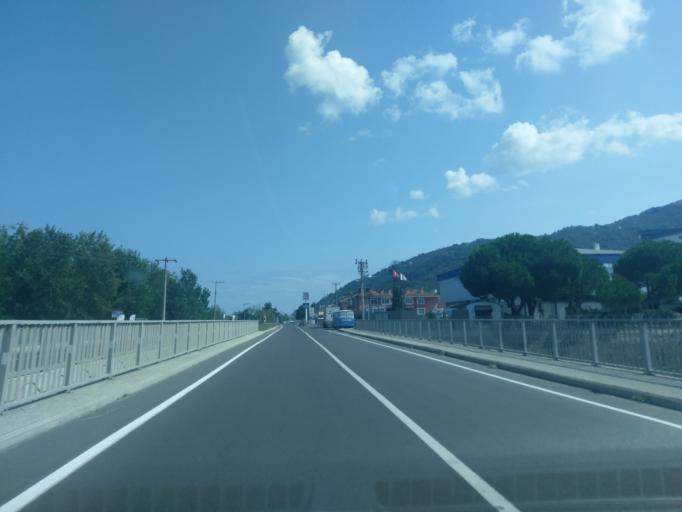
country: TR
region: Ordu
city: Ordu
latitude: 41.0198
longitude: 37.8305
